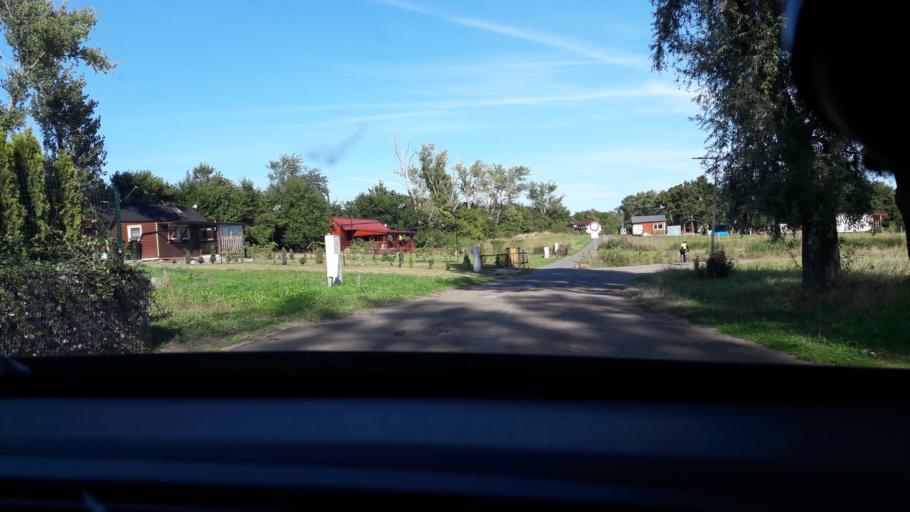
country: SK
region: Kosicky
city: Vinne
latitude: 48.8104
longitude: 22.0380
